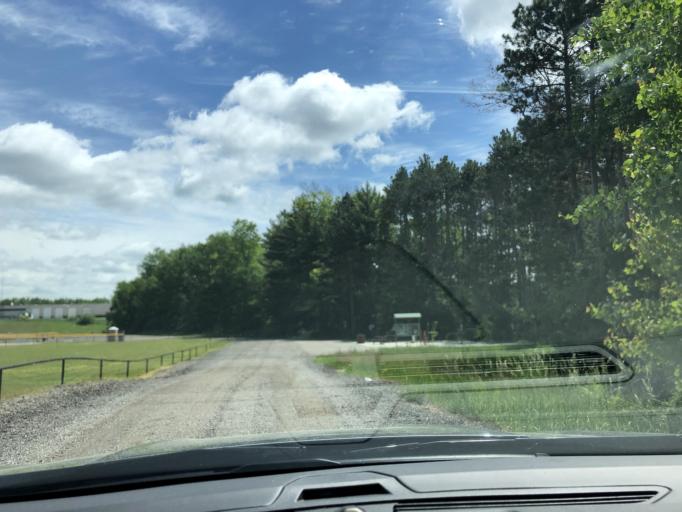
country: US
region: Michigan
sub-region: Clare County
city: Harrison
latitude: 44.0135
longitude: -84.8158
